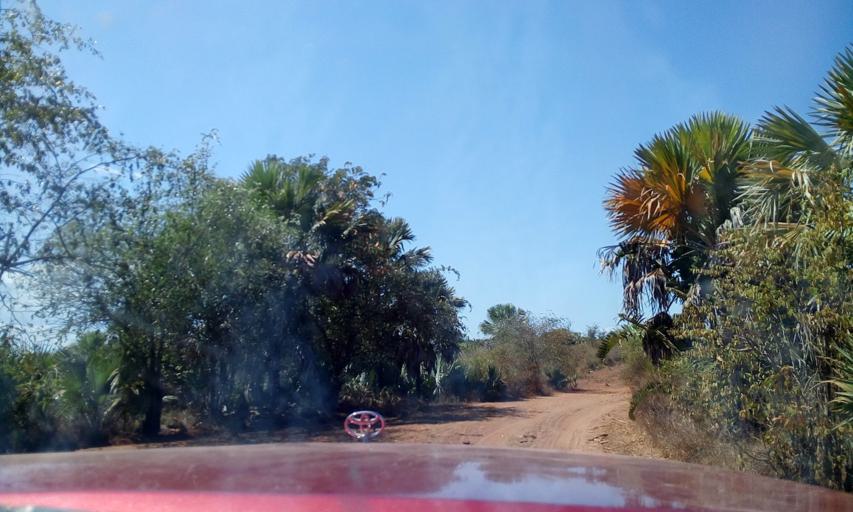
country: MG
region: Boeny
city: Sitampiky
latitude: -16.1167
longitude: 45.4686
